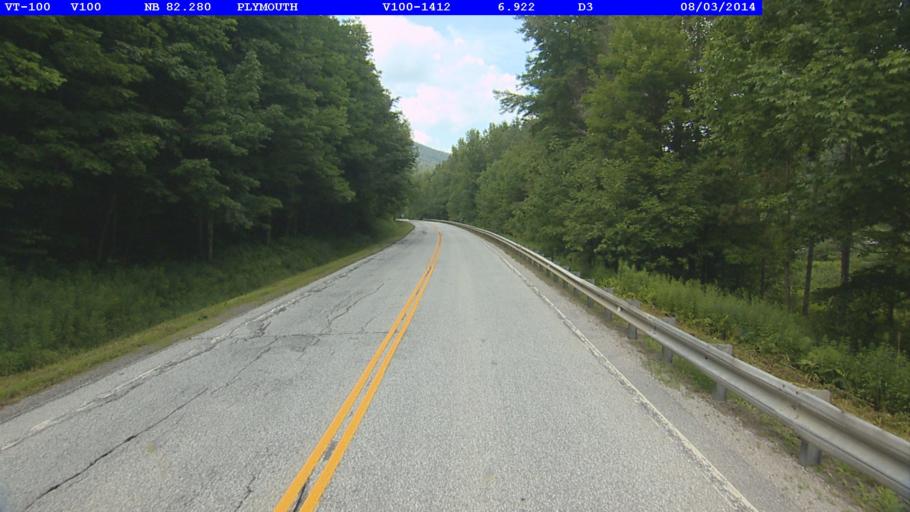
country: US
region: Vermont
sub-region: Rutland County
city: Rutland
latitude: 43.5500
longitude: -72.7537
